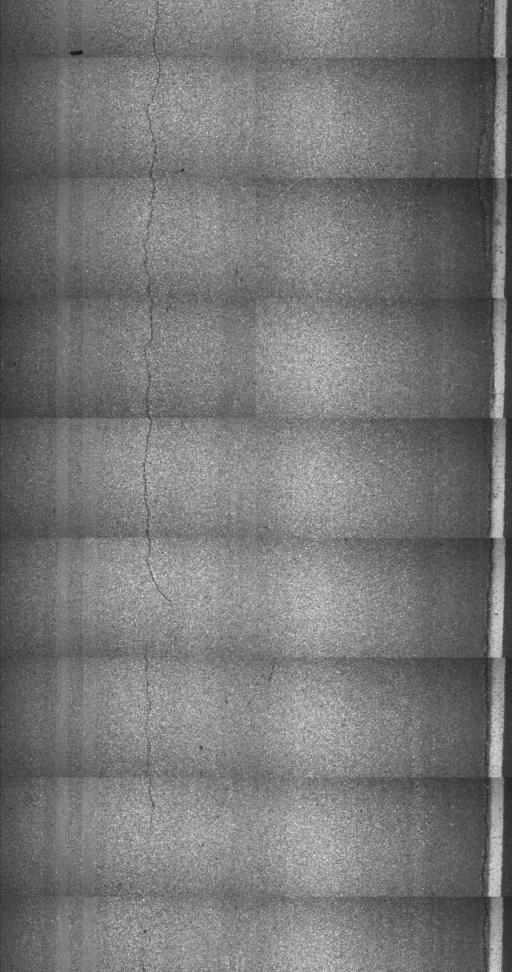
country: US
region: Vermont
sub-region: Rutland County
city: Rutland
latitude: 43.5537
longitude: -72.9583
